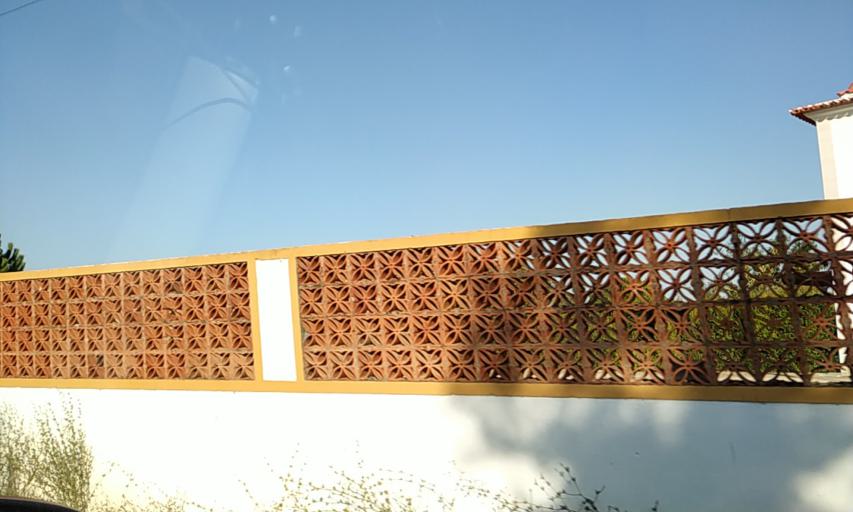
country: PT
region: Santarem
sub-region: Santarem
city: Santarem
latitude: 39.2605
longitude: -8.6672
